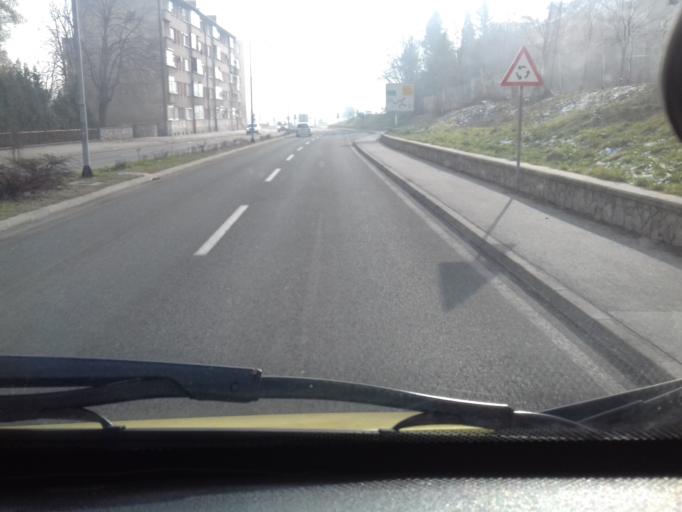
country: BA
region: Federation of Bosnia and Herzegovina
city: Zenica
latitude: 44.1925
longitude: 17.9170
